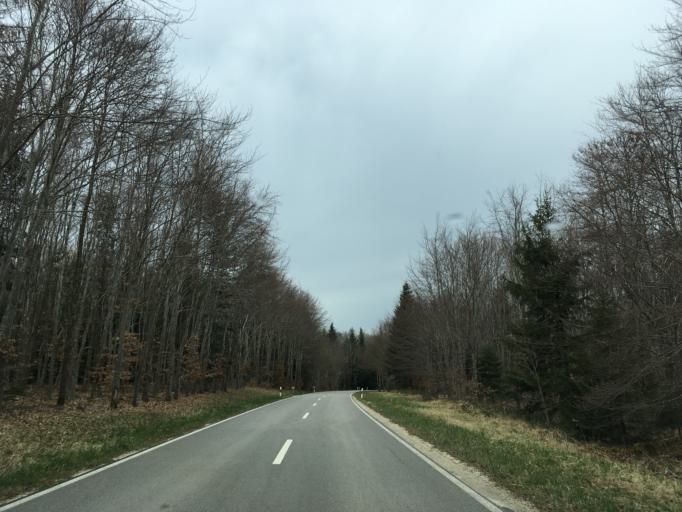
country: DE
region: Bavaria
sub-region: Upper Bavaria
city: Jettenbach
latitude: 48.1173
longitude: 12.3958
